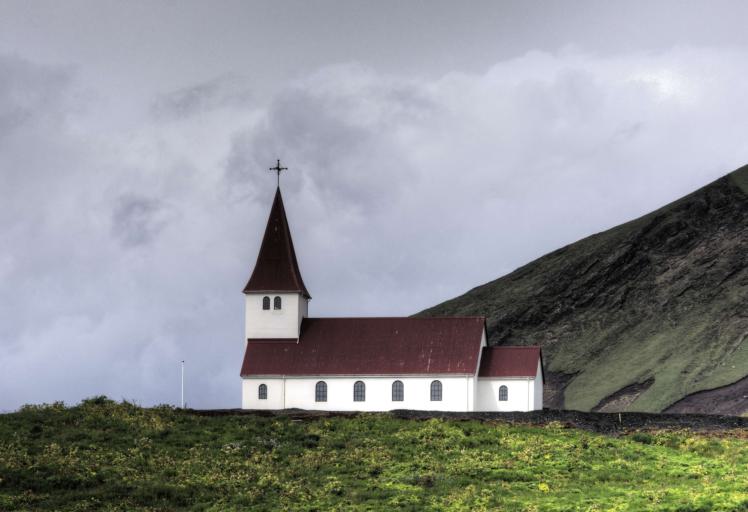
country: IS
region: South
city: Vestmannaeyjar
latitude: 63.4174
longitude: -19.0010
